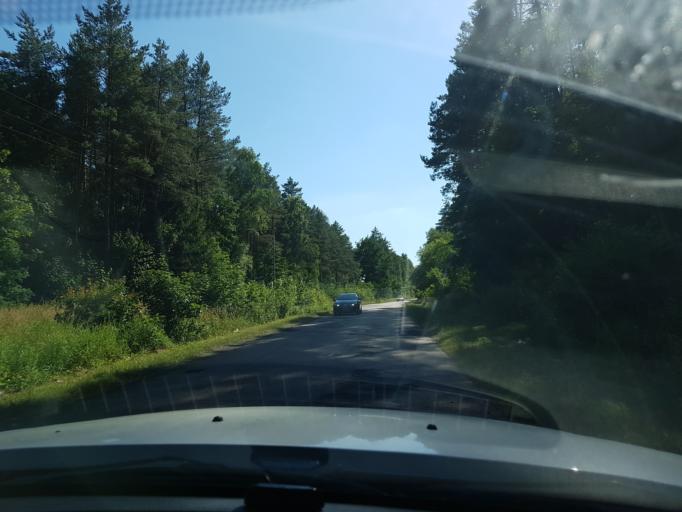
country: PL
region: West Pomeranian Voivodeship
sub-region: Powiat swidwinski
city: Slawoborze
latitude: 53.9182
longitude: 15.7879
